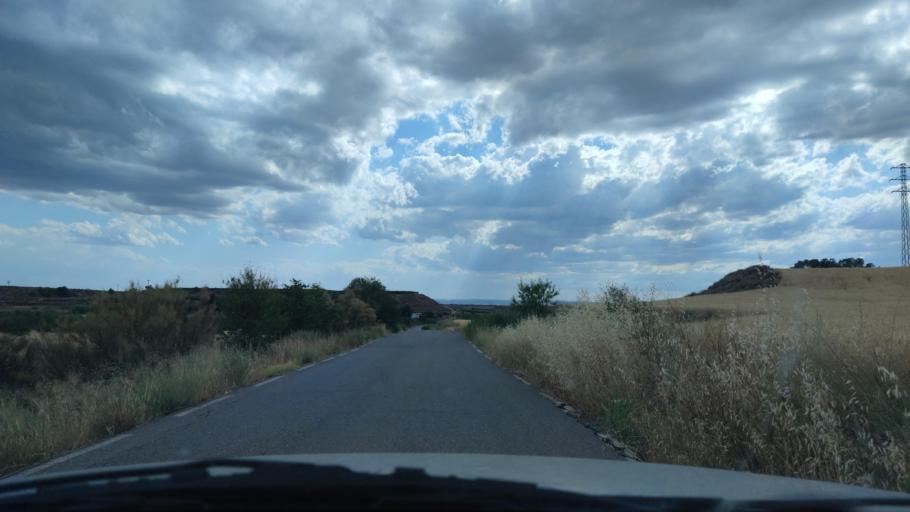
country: ES
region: Catalonia
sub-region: Provincia de Lleida
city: Lleida
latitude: 41.5976
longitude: 0.5791
